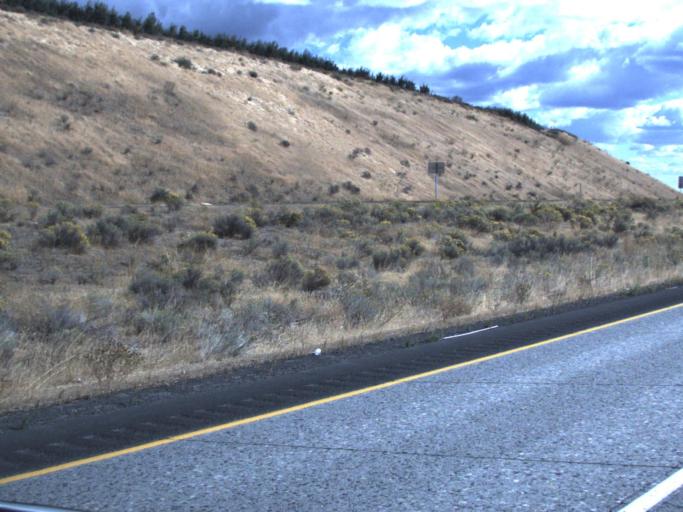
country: US
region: Washington
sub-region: Yakima County
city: Union Gap
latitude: 46.5050
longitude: -120.4501
